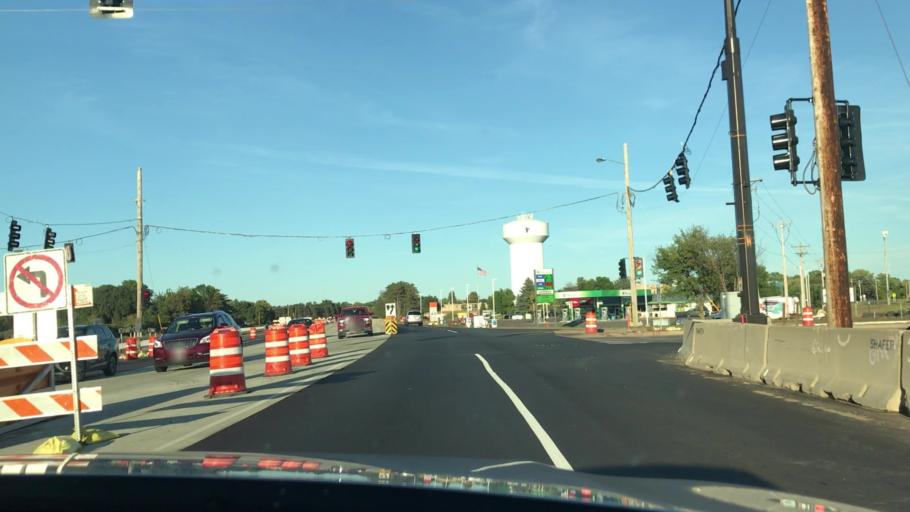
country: US
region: Minnesota
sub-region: Wright County
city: Otsego
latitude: 45.3064
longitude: -93.6094
